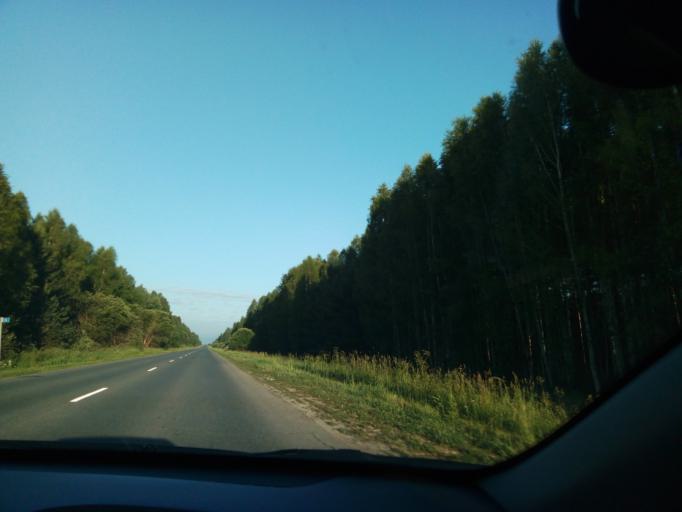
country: RU
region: Nizjnij Novgorod
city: Satis
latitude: 54.8950
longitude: 43.1067
